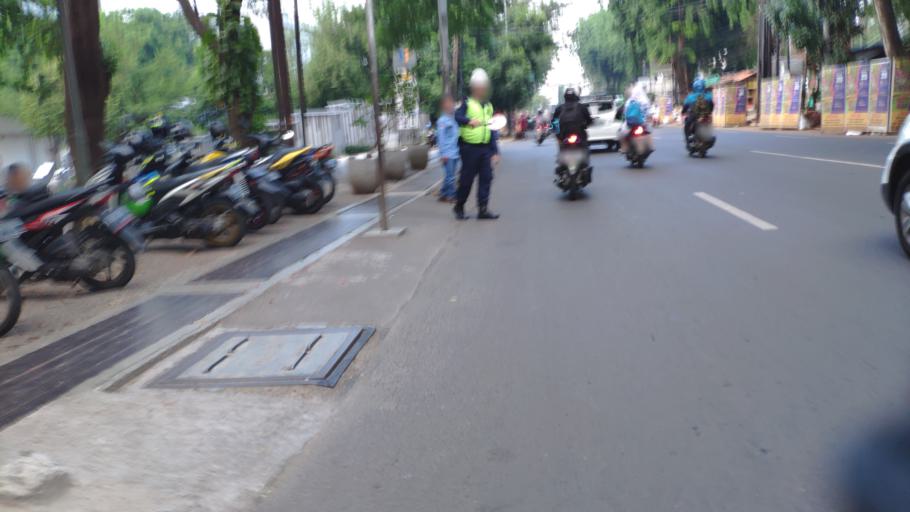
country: ID
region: Jakarta Raya
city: Jakarta
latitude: -6.2946
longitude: 106.8159
